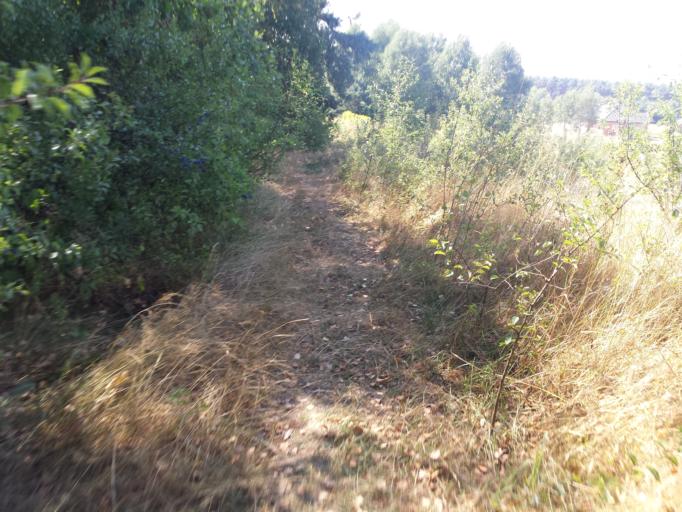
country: PL
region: Swietokrzyskie
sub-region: Powiat kielecki
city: Daleszyce
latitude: 50.8021
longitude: 20.7694
